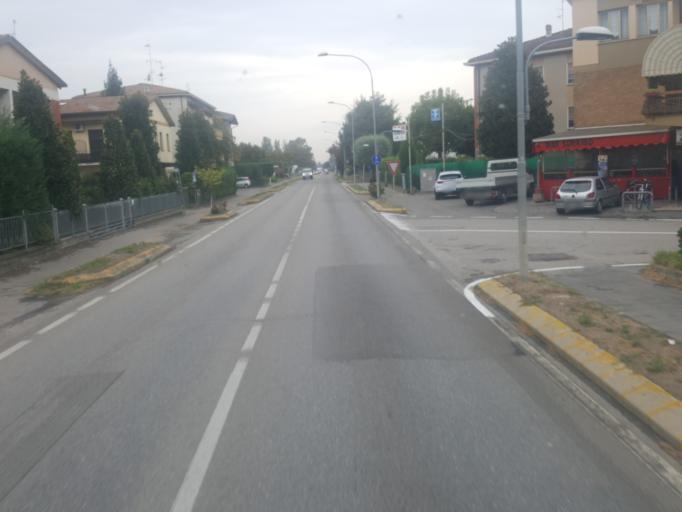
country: IT
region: Emilia-Romagna
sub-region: Provincia di Modena
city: Nonantola
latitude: 44.6780
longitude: 11.0301
